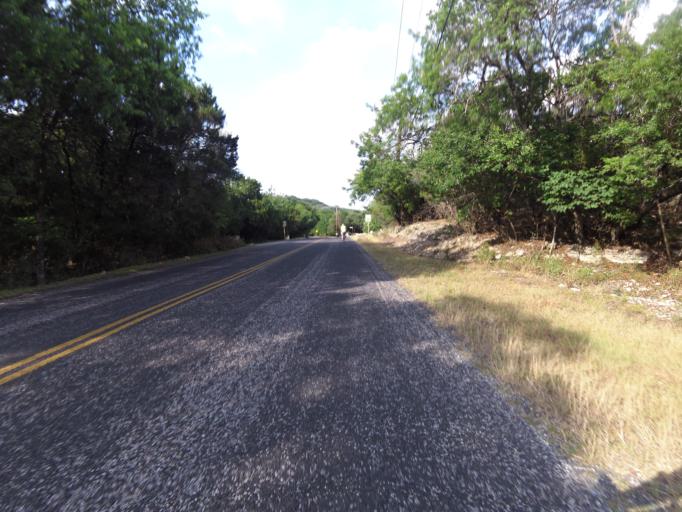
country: US
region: Texas
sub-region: Bexar County
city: Cross Mountain
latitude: 29.6460
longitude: -98.6435
